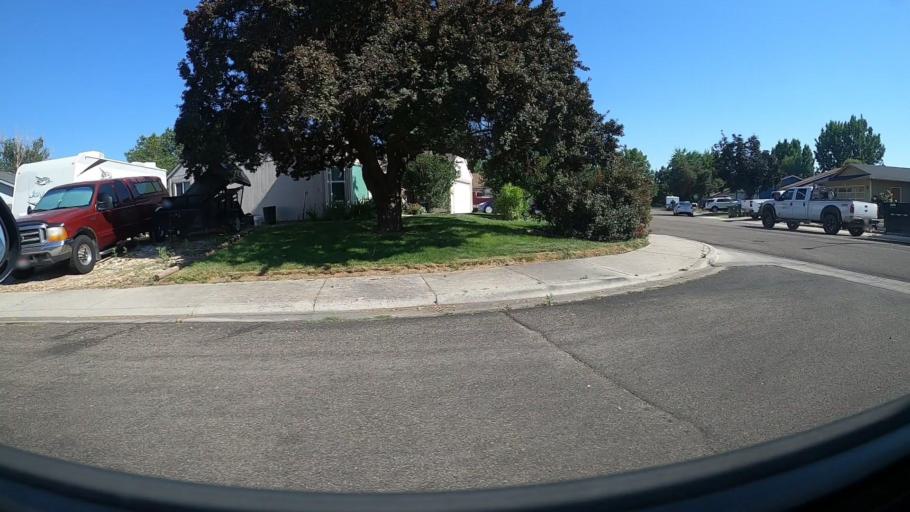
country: US
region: Idaho
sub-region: Ada County
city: Meridian
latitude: 43.6296
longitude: -116.4100
